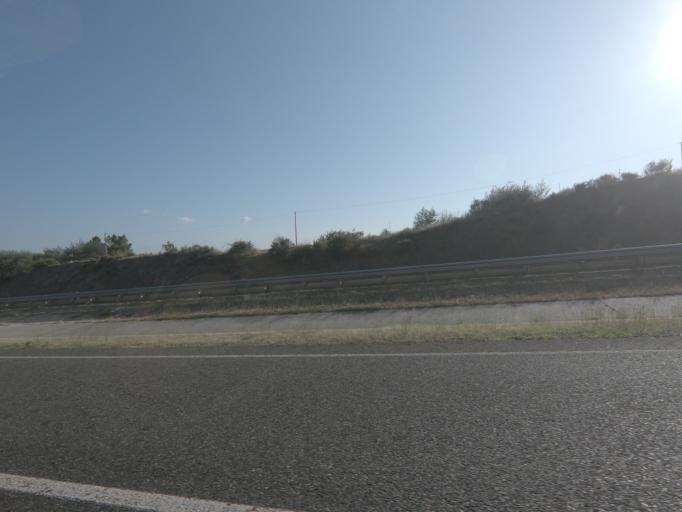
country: ES
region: Galicia
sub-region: Provincia de Ourense
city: Oimbra
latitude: 41.8499
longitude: -7.4130
